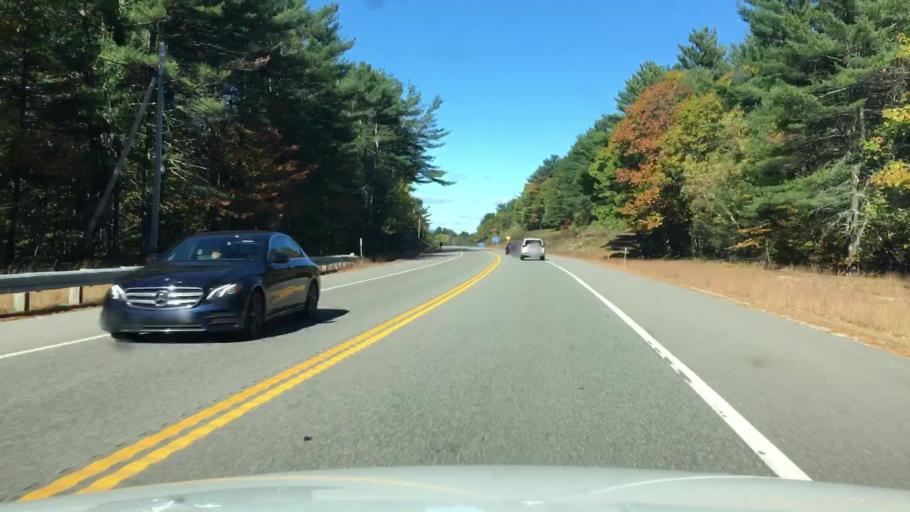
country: US
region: New Hampshire
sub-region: Carroll County
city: Sanbornville
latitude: 43.5429
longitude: -71.0343
